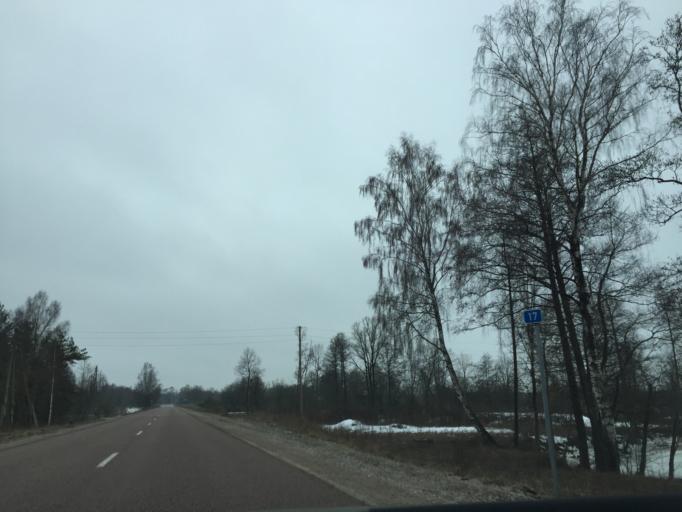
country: LV
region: Olaine
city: Olaine
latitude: 56.6319
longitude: 23.9342
